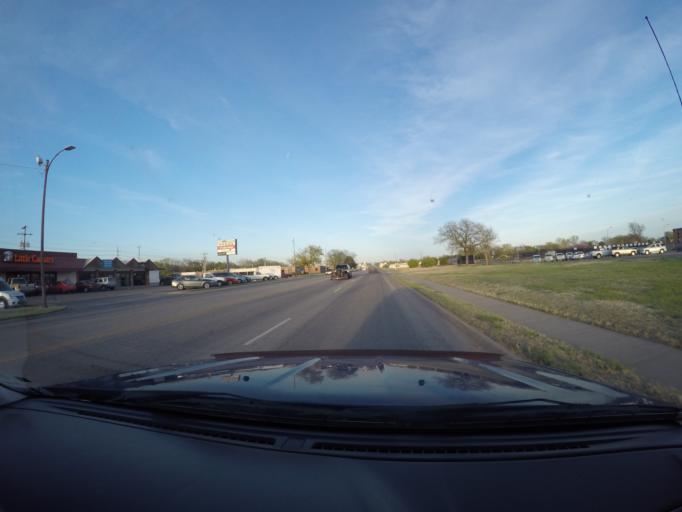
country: US
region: Kansas
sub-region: Saline County
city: Salina
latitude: 38.8271
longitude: -97.6016
